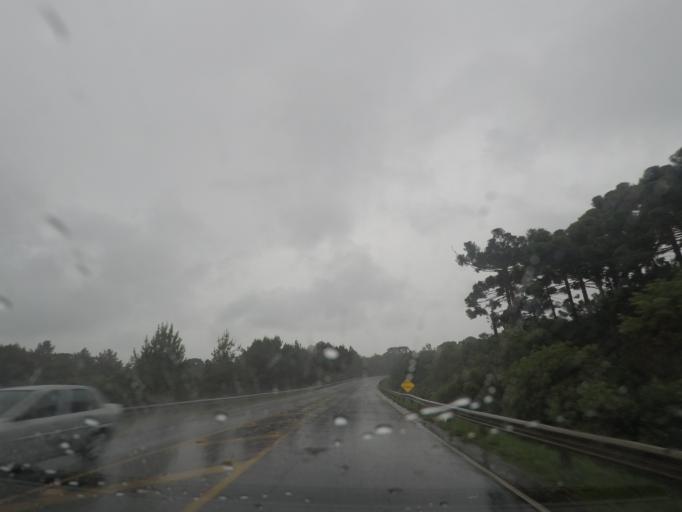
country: BR
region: Parana
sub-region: Almirante Tamandare
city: Almirante Tamandare
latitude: -25.3553
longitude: -49.3081
